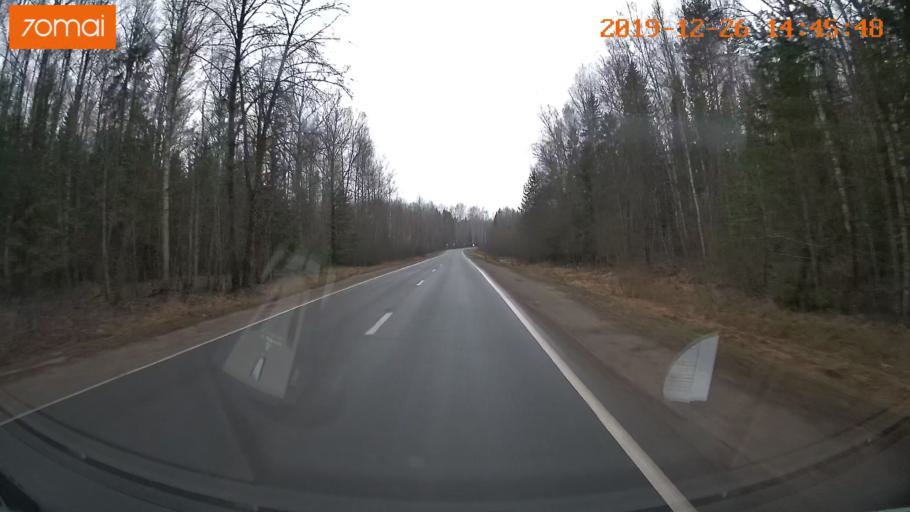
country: RU
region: Jaroslavl
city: Poshekhon'ye
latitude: 58.3357
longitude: 39.0311
